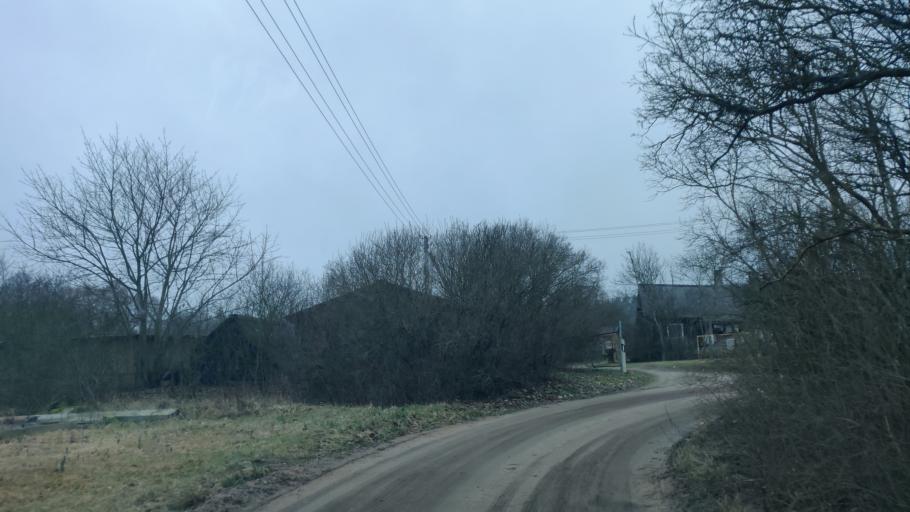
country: LT
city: Trakai
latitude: 54.5603
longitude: 24.9281
